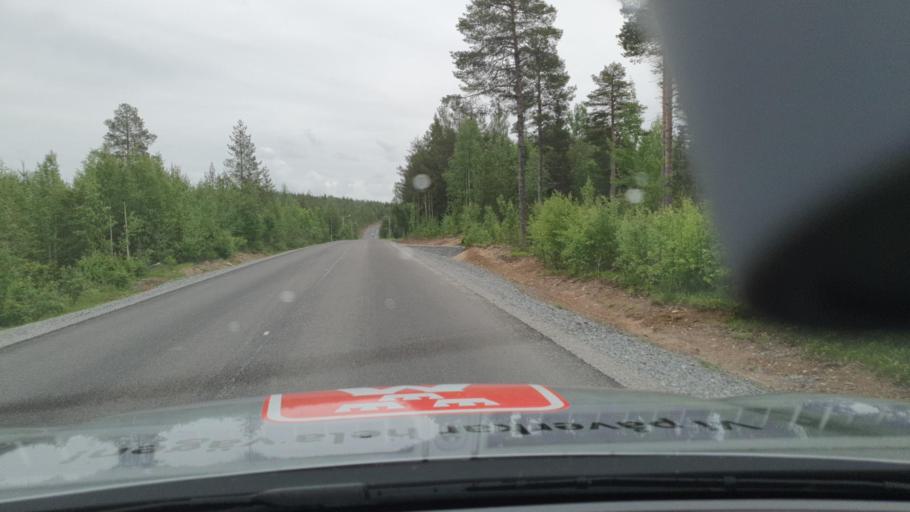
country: SE
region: Norrbotten
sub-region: Overtornea Kommun
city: OEvertornea
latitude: 66.6046
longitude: 23.2998
